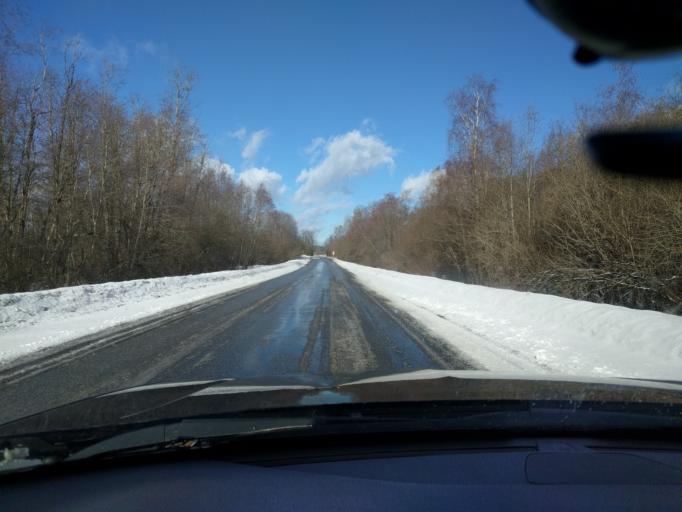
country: EE
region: Harju
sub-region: Raasiku vald
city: Raasiku
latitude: 59.3059
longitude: 25.1692
